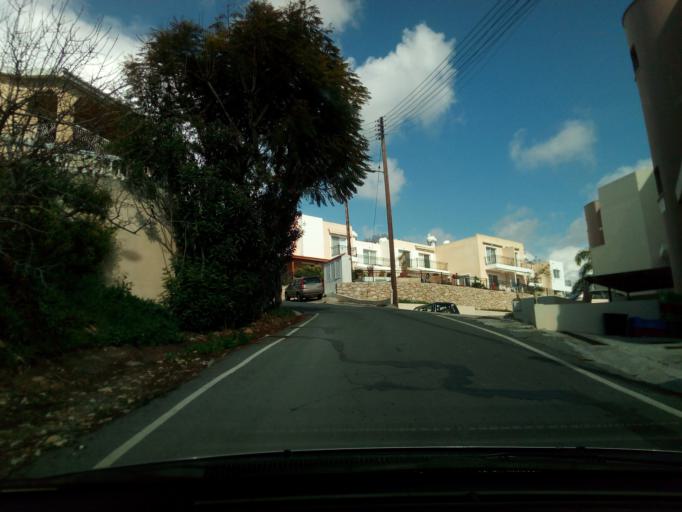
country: CY
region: Pafos
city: Mesogi
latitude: 34.8150
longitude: 32.4460
